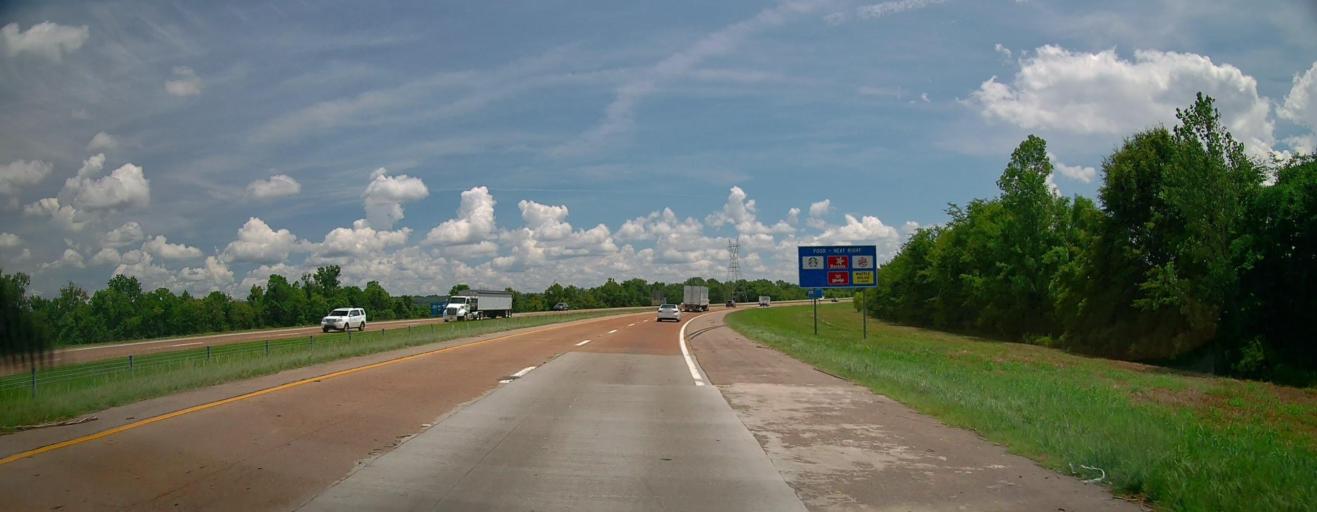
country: US
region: Mississippi
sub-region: Lee County
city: Tupelo
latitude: 34.2678
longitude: -88.6956
